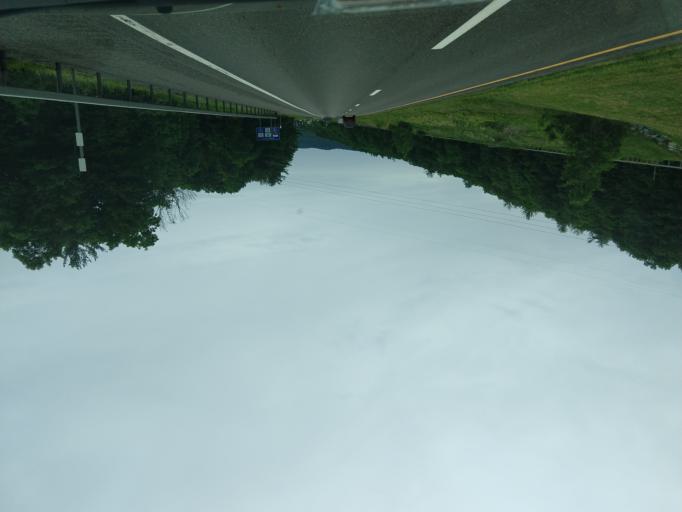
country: US
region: New York
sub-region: Broome County
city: Chenango Bridge
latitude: 42.1775
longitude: -75.8995
